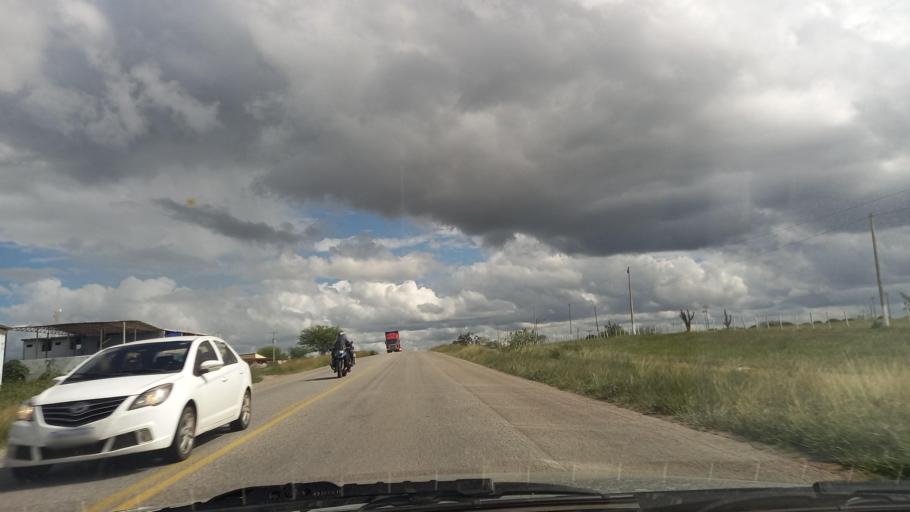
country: BR
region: Pernambuco
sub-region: Cachoeirinha
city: Cachoeirinha
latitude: -8.5078
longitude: -36.2504
